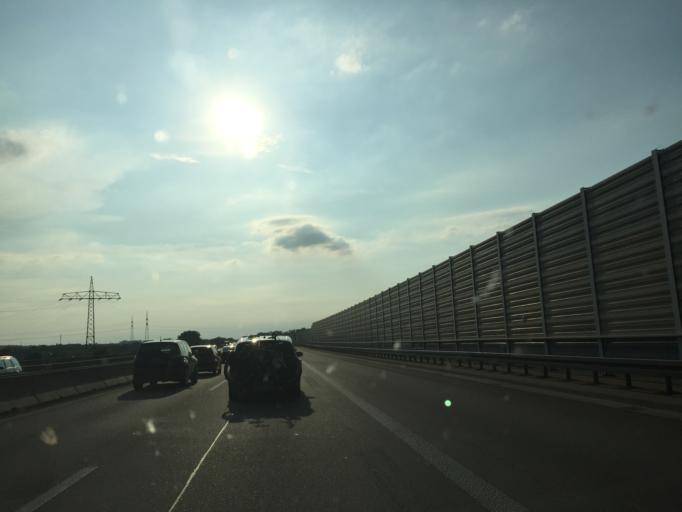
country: DE
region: Baden-Wuerttemberg
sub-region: Regierungsbezirk Stuttgart
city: Neckarsulm
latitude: 49.1843
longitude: 9.2157
